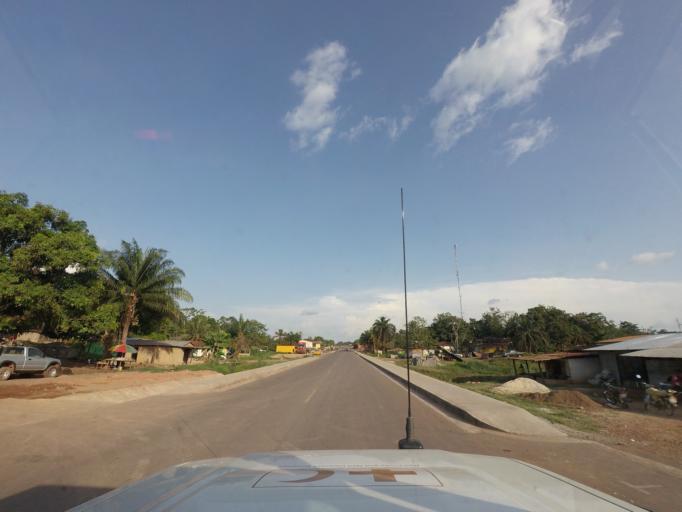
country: LR
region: Bong
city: Gbarnga
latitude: 6.9983
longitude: -9.4700
